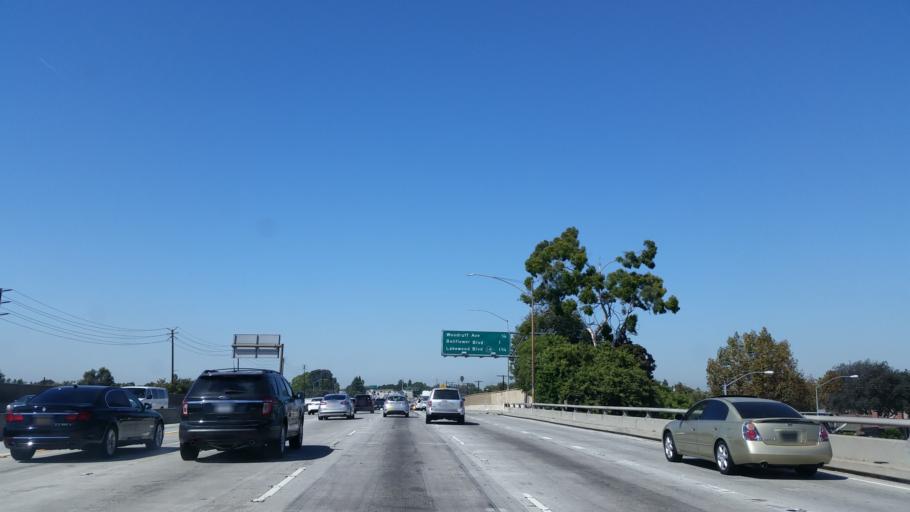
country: US
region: California
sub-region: Orange County
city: Rossmoor
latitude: 33.7969
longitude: -118.1077
